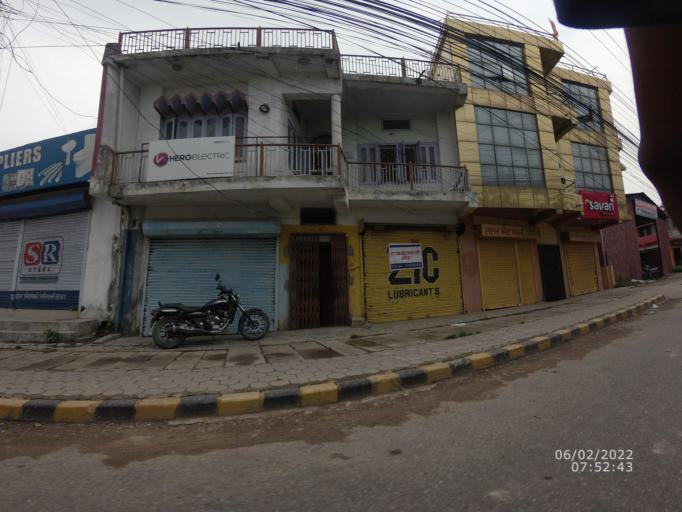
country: NP
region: Western Region
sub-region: Lumbini Zone
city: Bhairahawa
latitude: 27.5107
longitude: 83.4550
